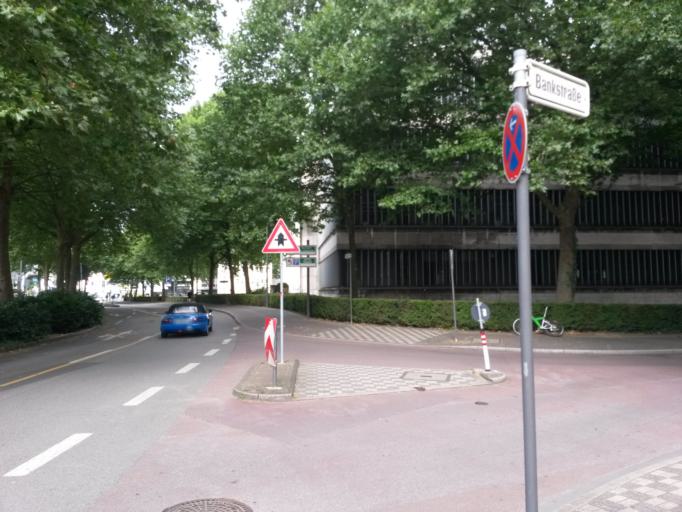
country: DE
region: North Rhine-Westphalia
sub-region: Regierungsbezirk Dusseldorf
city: Wuppertal
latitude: 51.2560
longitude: 7.1444
